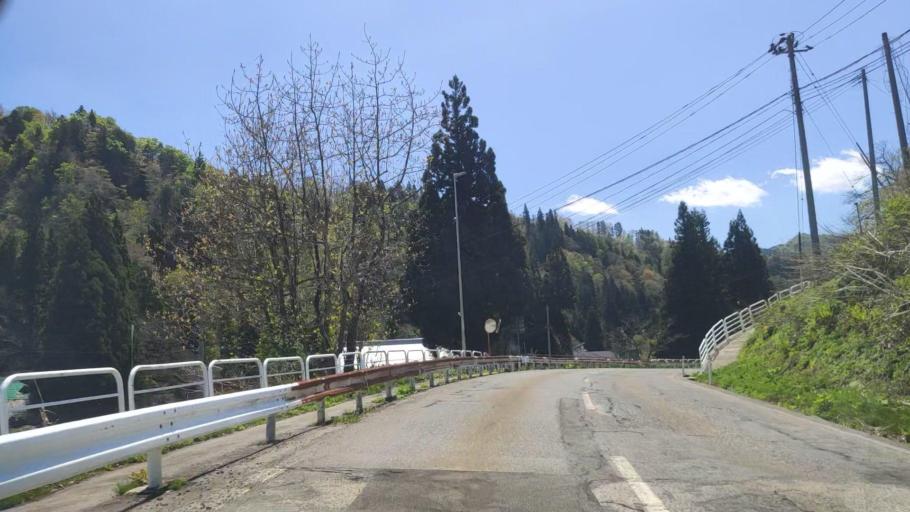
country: JP
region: Yamagata
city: Shinjo
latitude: 38.9810
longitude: 140.3622
